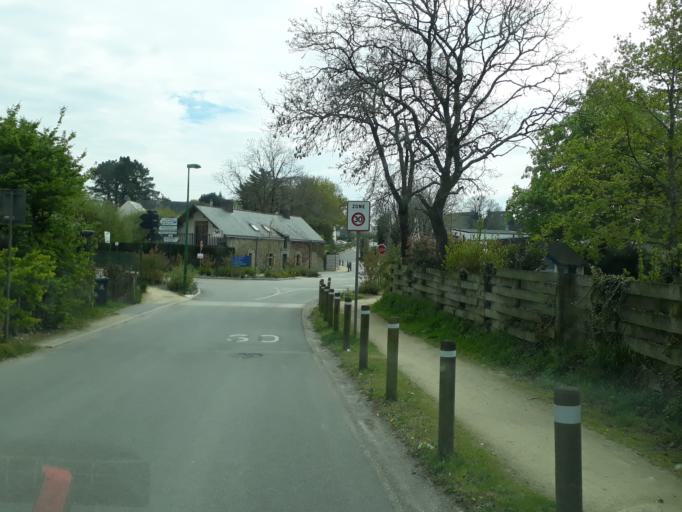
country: FR
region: Brittany
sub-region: Departement du Morbihan
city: Surzur
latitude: 47.5812
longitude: -2.6347
